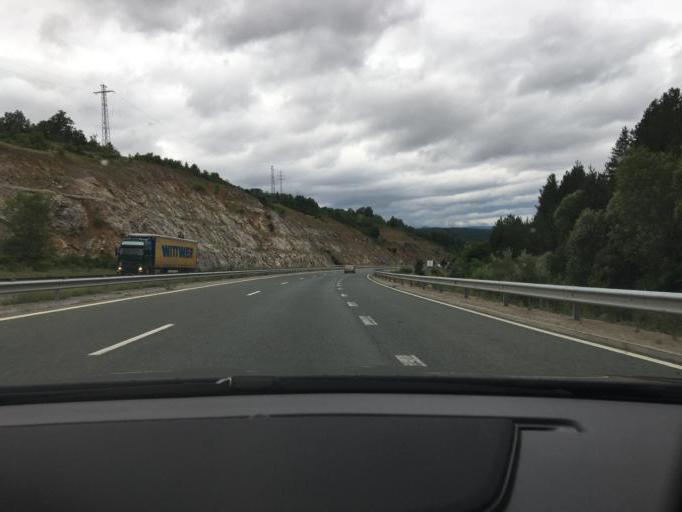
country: BG
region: Pernik
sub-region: Obshtina Pernik
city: Pernik
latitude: 42.4933
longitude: 23.1337
